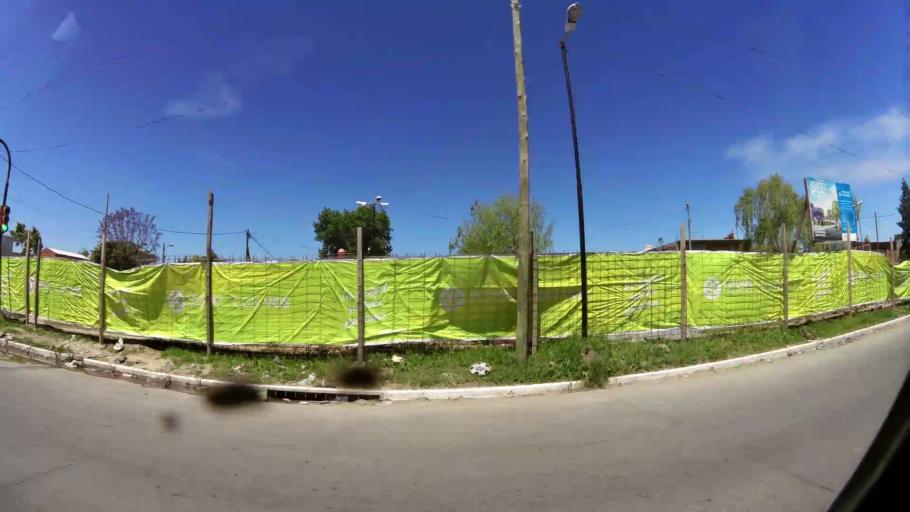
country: AR
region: Buenos Aires
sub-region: Partido de Lanus
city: Lanus
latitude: -34.7234
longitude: -58.3296
